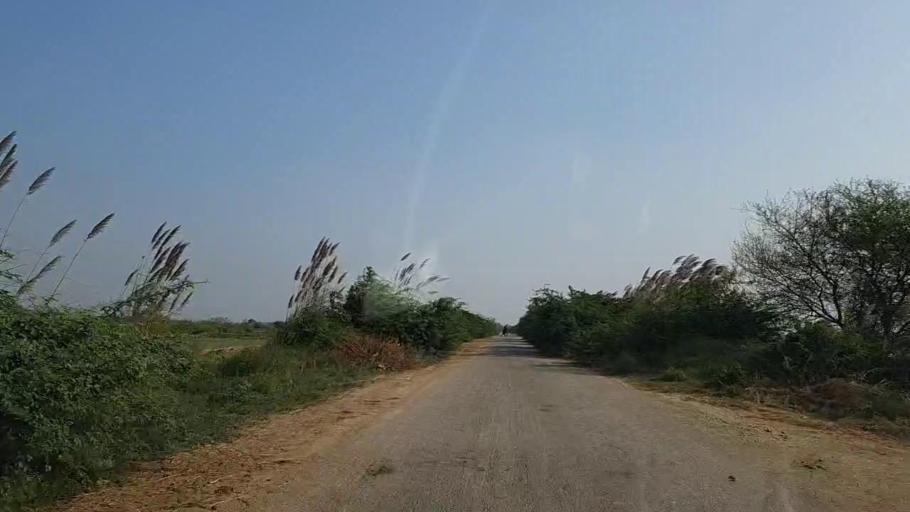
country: PK
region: Sindh
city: Mirpur Sakro
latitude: 24.6249
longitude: 67.6552
